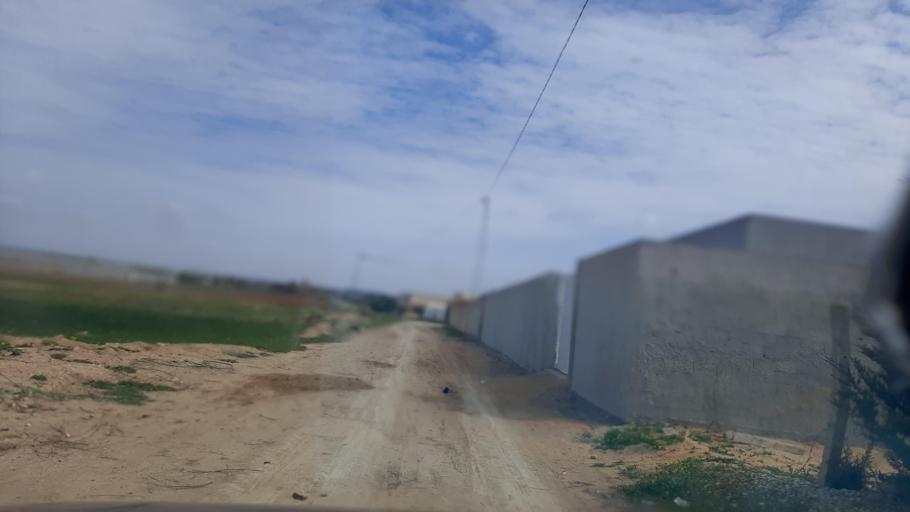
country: TN
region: Tunis
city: Oued Lill
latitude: 36.6931
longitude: 9.9967
